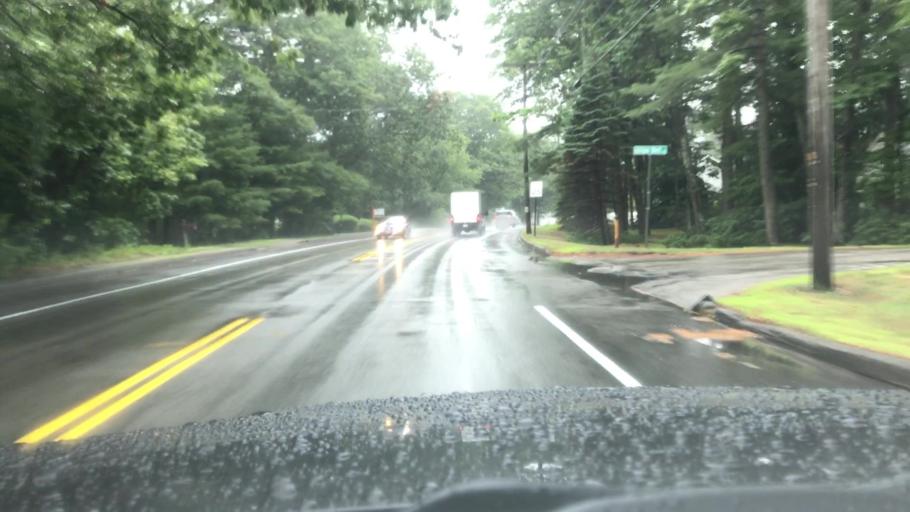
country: US
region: Maine
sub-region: York County
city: Kennebunk
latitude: 43.4013
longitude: -70.5564
